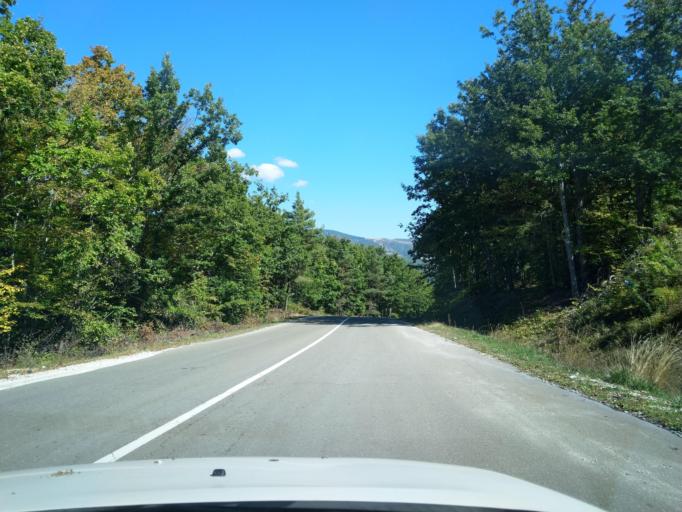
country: RS
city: Sokolovica
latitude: 43.2532
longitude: 20.2475
